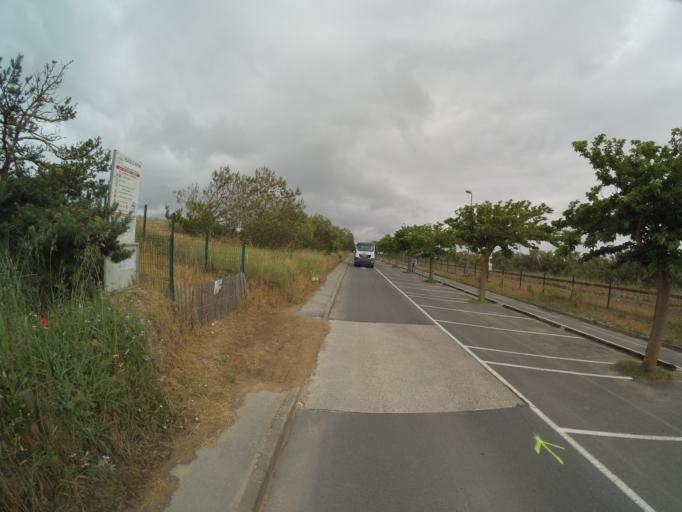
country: FR
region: Poitou-Charentes
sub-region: Departement de la Charente-Maritime
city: Aytre
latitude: 46.1239
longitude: -1.1257
